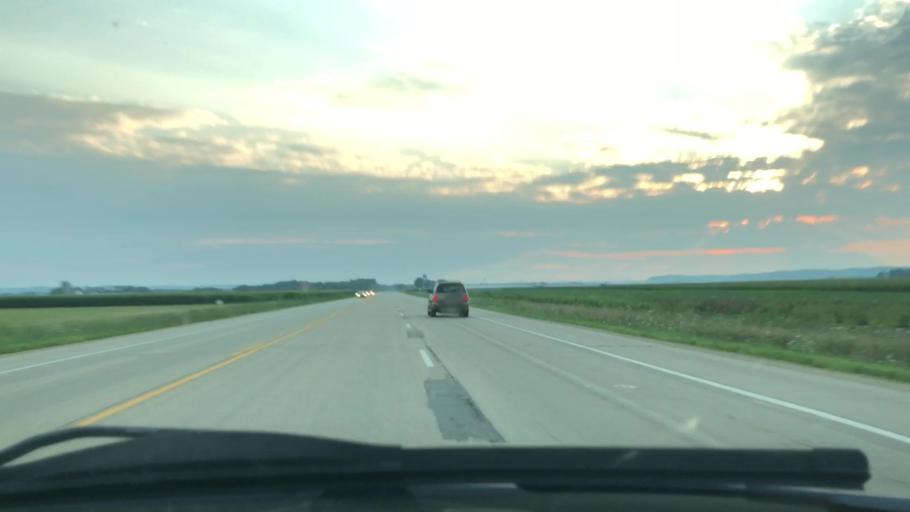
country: US
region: Wisconsin
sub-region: Sauk County
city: Spring Green
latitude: 43.1899
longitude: -90.1047
